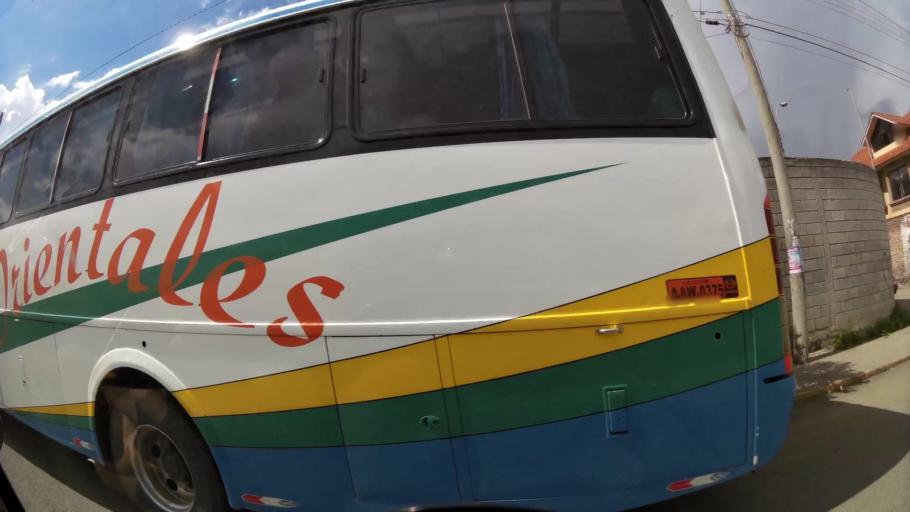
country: EC
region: Azuay
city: Cuenca
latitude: -2.8960
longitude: -78.9939
